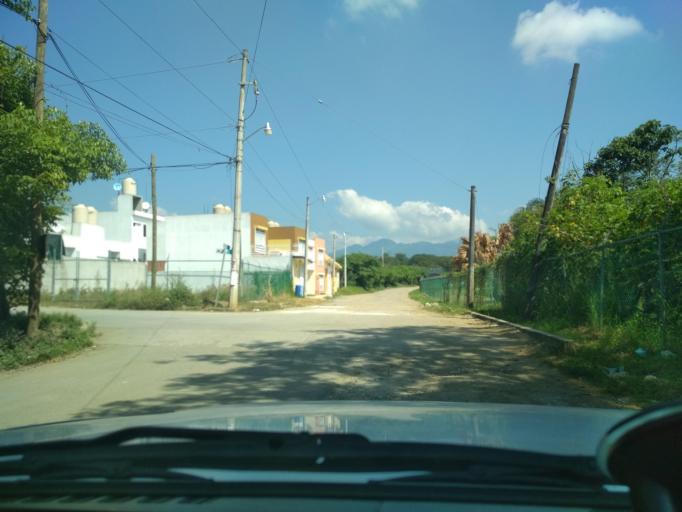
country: MX
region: Veracruz
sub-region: Fortin
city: Fraccionamiento Villas de la Llave
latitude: 18.9156
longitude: -96.9845
